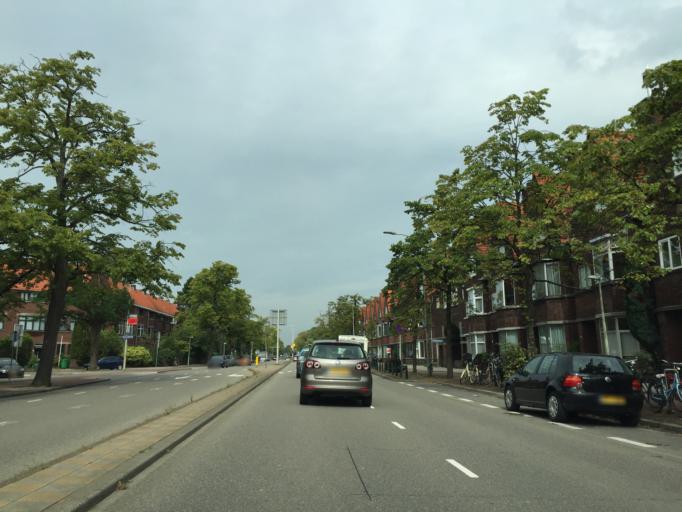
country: NL
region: South Holland
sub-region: Gemeente Den Haag
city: The Hague
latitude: 52.0935
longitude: 4.3294
